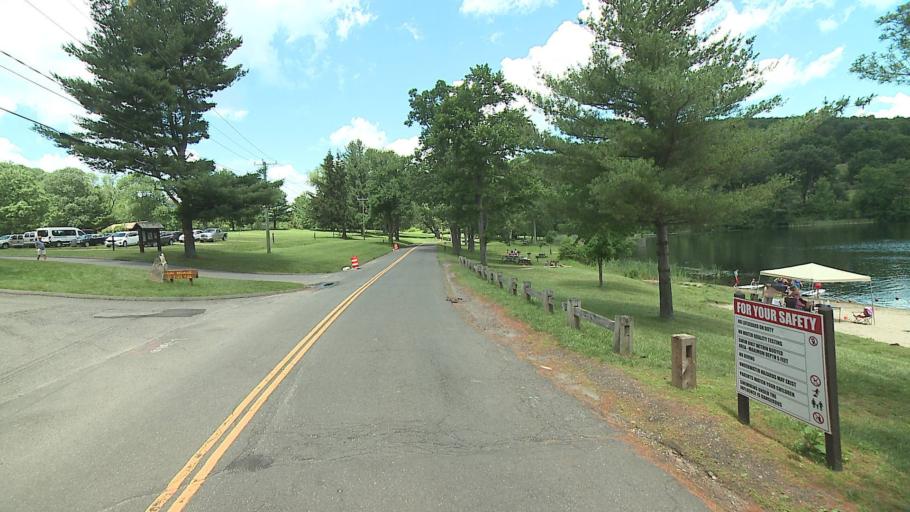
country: US
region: Connecticut
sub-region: Litchfield County
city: New Preston
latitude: 41.7078
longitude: -73.3836
